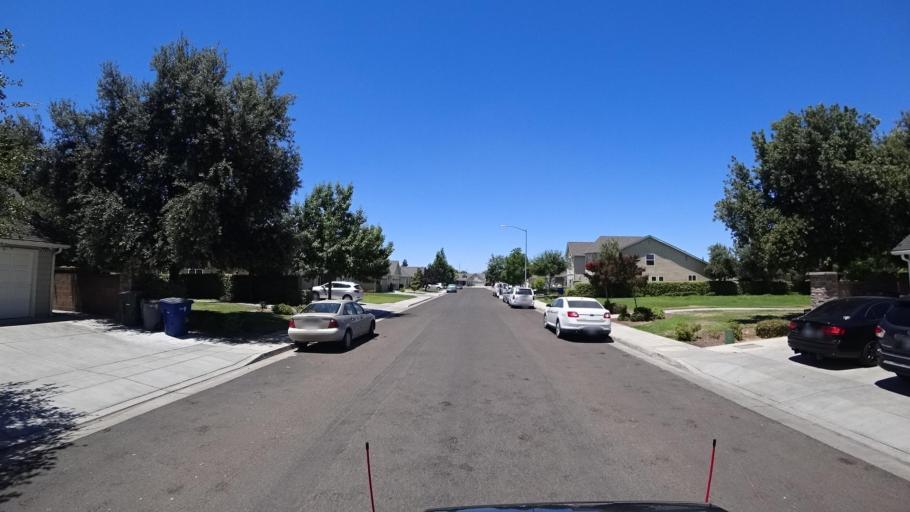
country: US
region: California
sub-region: Fresno County
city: Sunnyside
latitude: 36.7349
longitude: -119.6706
